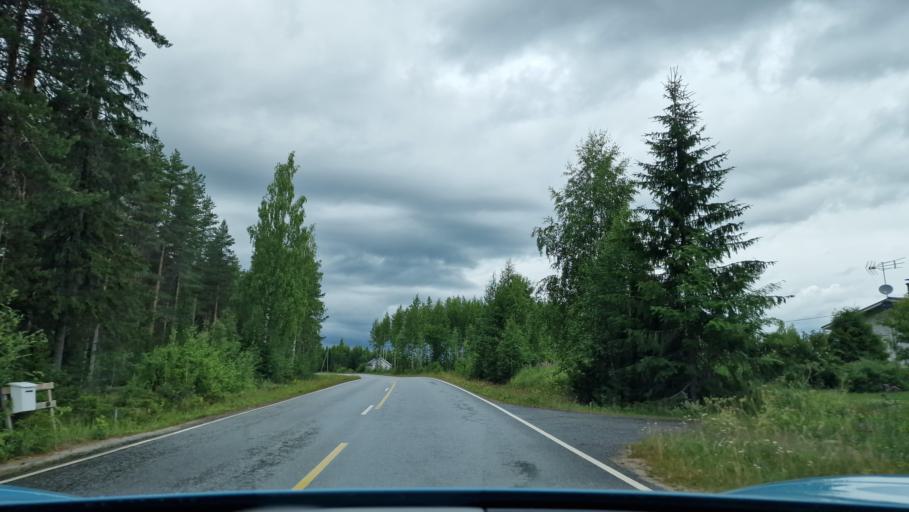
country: FI
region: Southern Ostrobothnia
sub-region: Jaerviseutu
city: Soini
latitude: 62.7169
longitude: 24.4367
